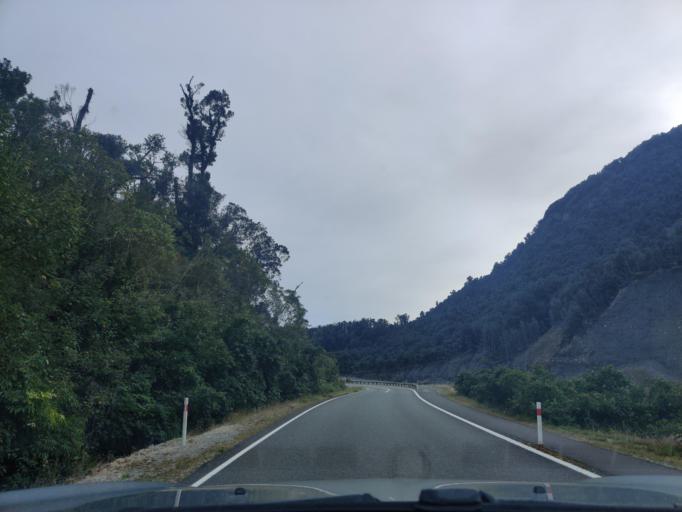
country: NZ
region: West Coast
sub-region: Westland District
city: Hokitika
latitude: -43.3986
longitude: 170.1810
